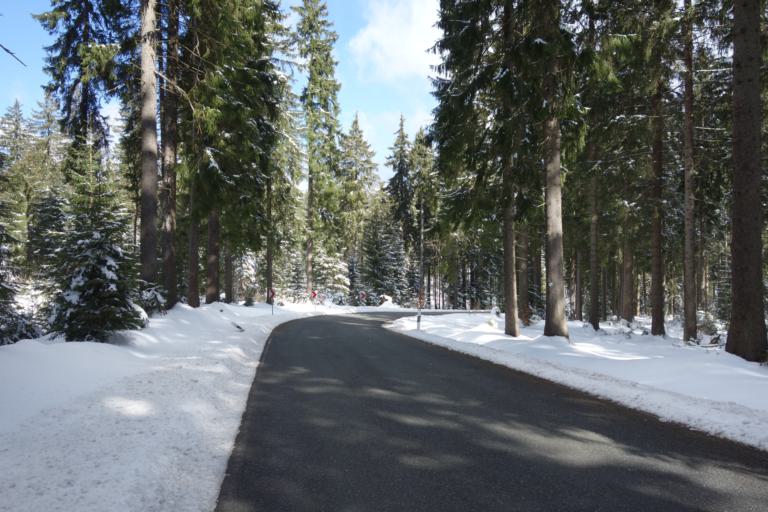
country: DE
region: Saxony
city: Eibenstock
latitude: 50.4379
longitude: 12.6064
